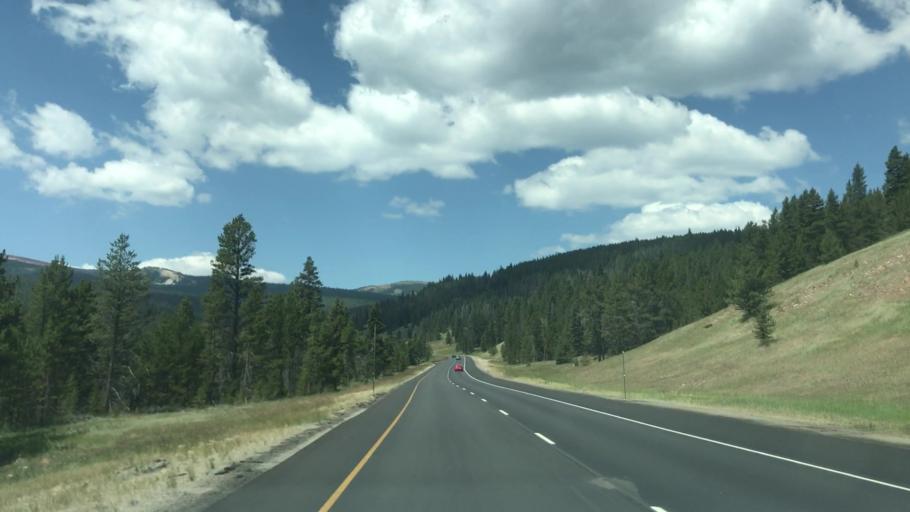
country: US
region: Colorado
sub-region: Summit County
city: Frisco
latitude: 39.5060
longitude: -106.1830
